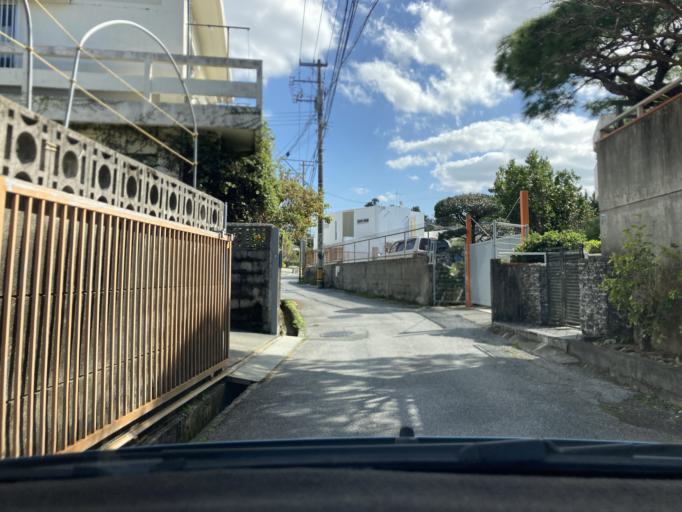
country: JP
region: Okinawa
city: Naha-shi
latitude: 26.2099
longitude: 127.7148
